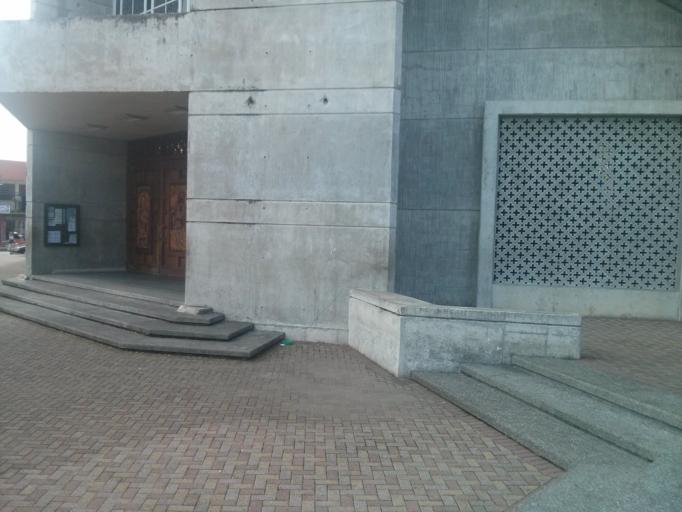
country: CR
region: Limon
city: Limon
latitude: 9.9930
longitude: -83.0306
